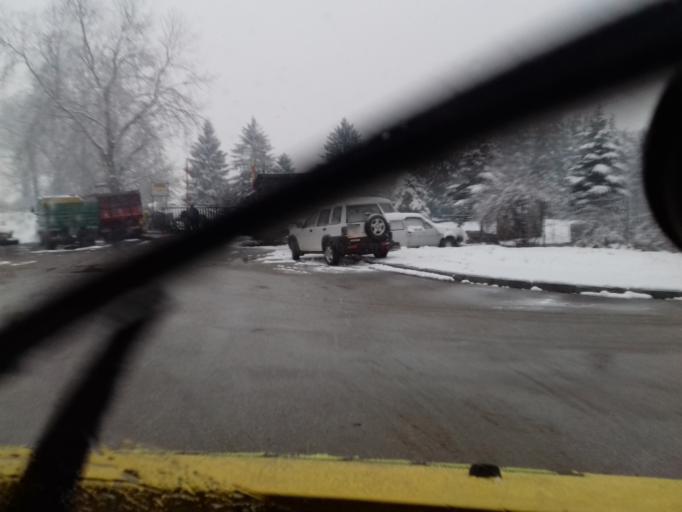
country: BA
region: Federation of Bosnia and Herzegovina
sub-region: Kanton Sarajevo
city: Sarajevo
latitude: 43.8138
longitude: 18.3283
